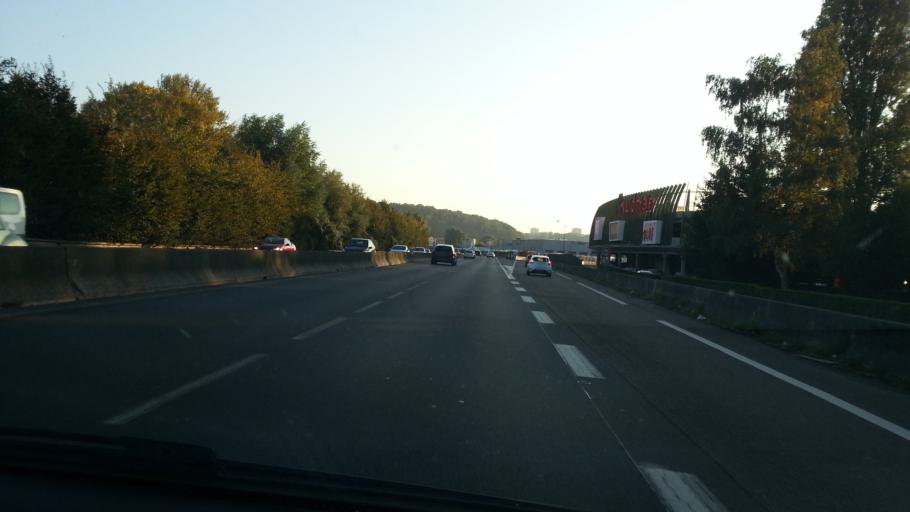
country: FR
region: Picardie
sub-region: Departement de l'Oise
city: Nogent-sur-Oise
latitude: 49.2719
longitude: 2.4857
